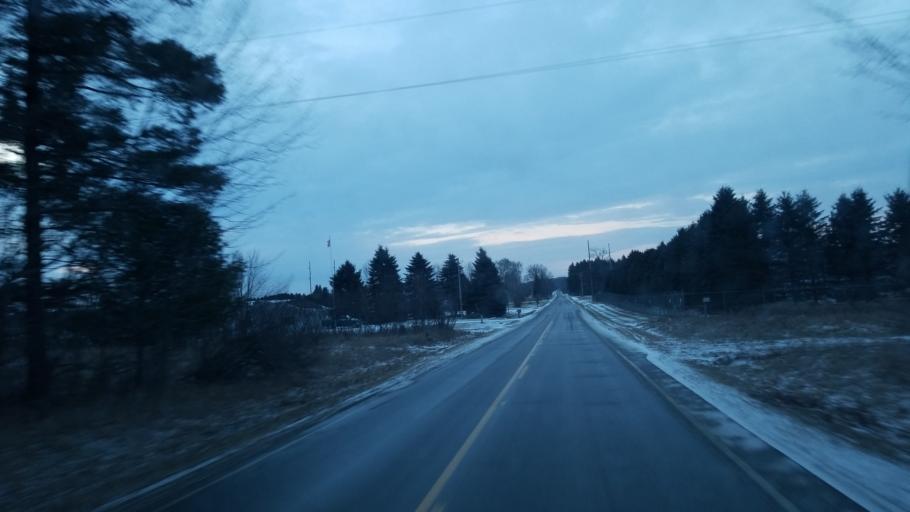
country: US
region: Michigan
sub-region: Osceola County
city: Reed City
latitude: 43.8406
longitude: -85.4242
